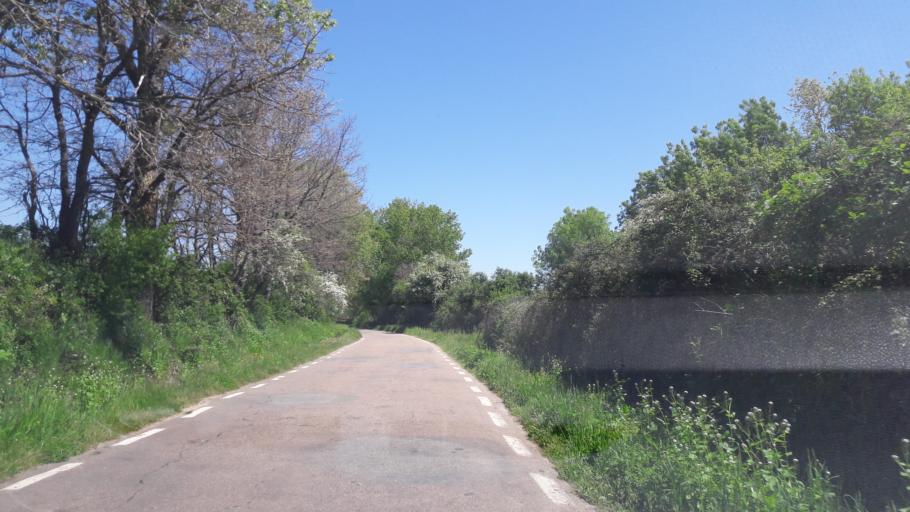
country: ES
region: Castille and Leon
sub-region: Provincia de Salamanca
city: Endrinal
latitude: 40.5865
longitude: -5.8044
